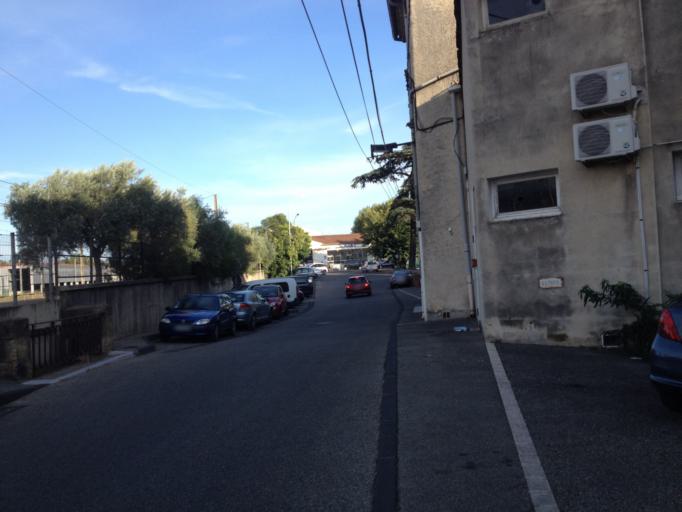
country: FR
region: Provence-Alpes-Cote d'Azur
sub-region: Departement du Vaucluse
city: Orange
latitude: 44.1380
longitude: 4.8180
